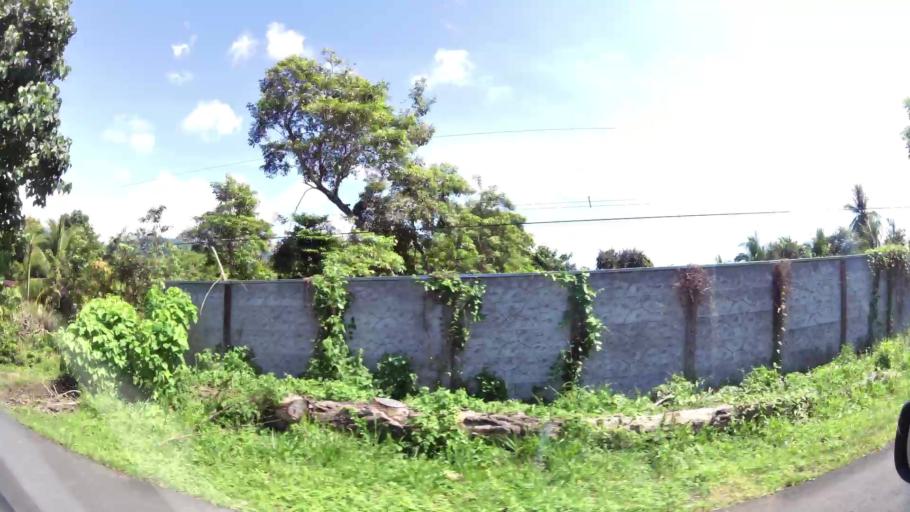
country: CR
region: Puntarenas
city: Quepos
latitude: 9.3264
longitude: -83.9580
